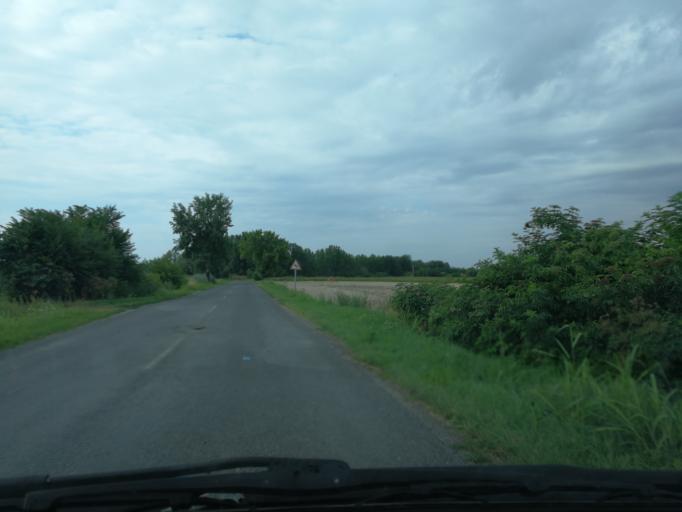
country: HU
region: Bacs-Kiskun
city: Batya
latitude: 46.4541
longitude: 19.0327
